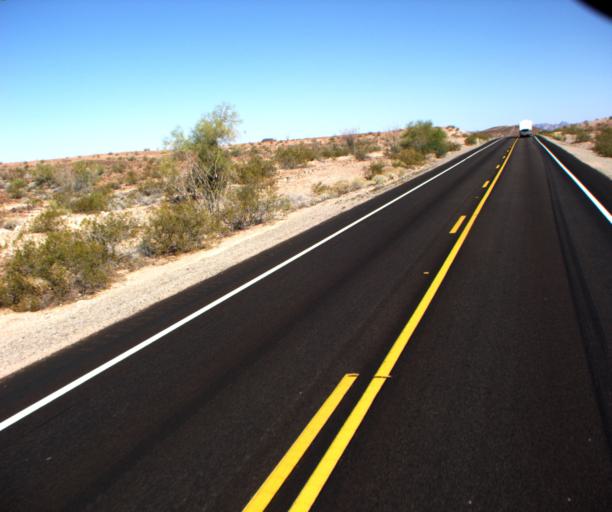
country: US
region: Arizona
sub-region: Yuma County
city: Wellton
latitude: 33.0889
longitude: -114.2968
